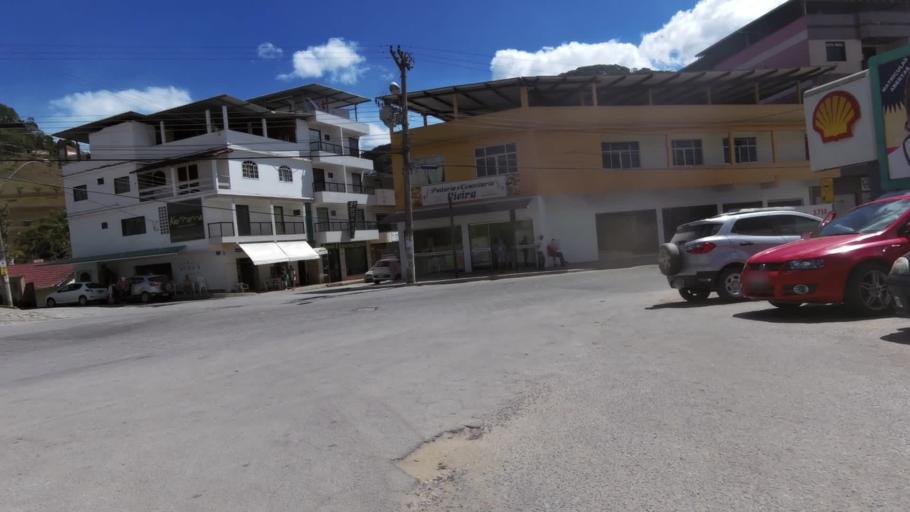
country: BR
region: Espirito Santo
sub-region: Vargem Alta
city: Vargem Alta
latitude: -20.6758
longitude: -41.0127
